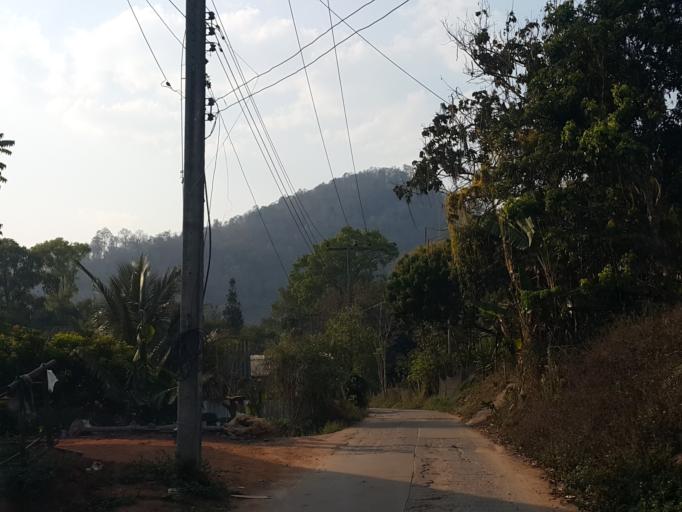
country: TH
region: Chiang Mai
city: Samoeng
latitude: 18.9006
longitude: 98.8311
